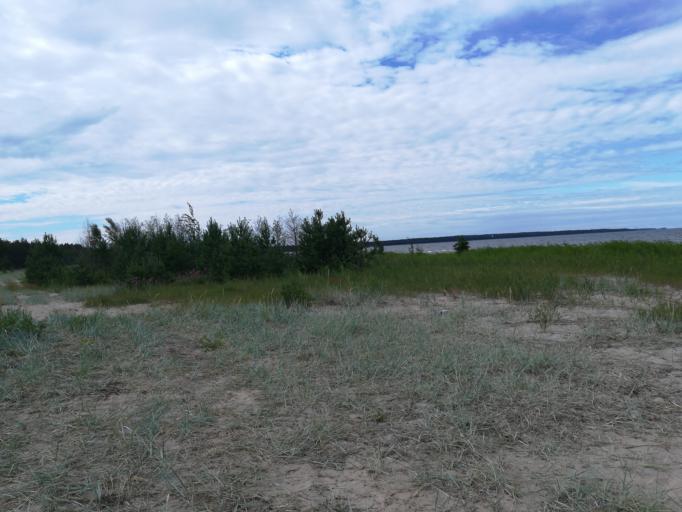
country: RU
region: Leningrad
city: Ust'-Luga
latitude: 59.6773
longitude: 28.2495
